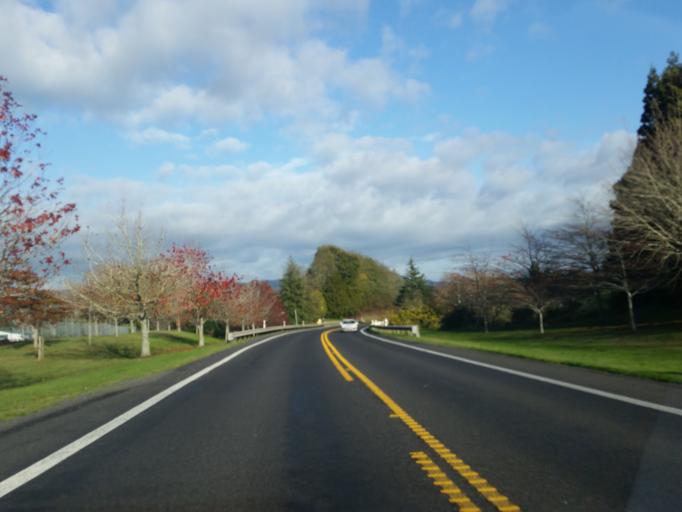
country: NZ
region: Waikato
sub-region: Hauraki District
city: Waihi
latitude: -37.4009
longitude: 175.8223
